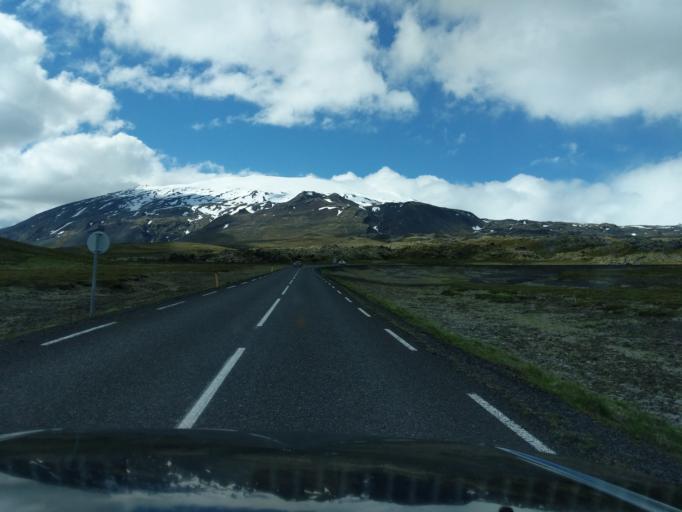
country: IS
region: West
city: Olafsvik
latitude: 64.7606
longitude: -23.6741
